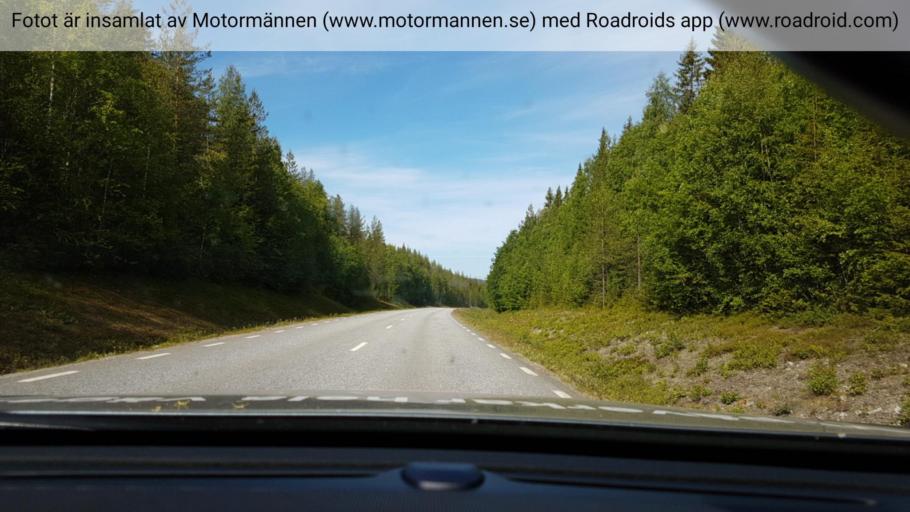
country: SE
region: Vaesterbotten
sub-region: Dorotea Kommun
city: Dorotea
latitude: 64.2373
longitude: 16.7614
